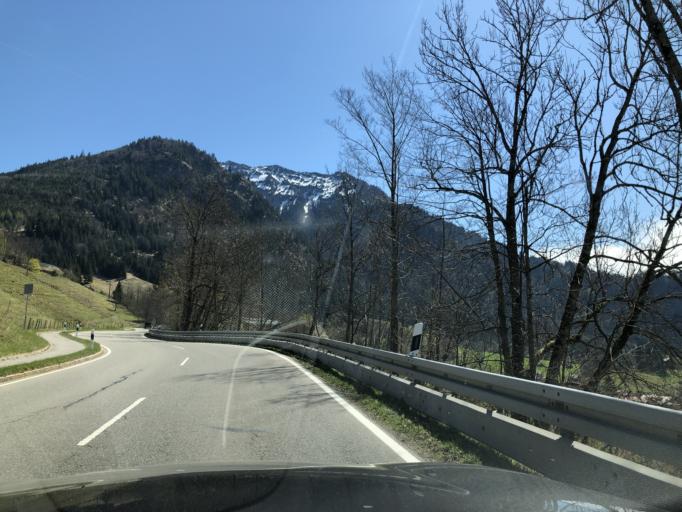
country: AT
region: Tyrol
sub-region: Politischer Bezirk Reutte
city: Schattwald
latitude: 47.5067
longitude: 10.3832
